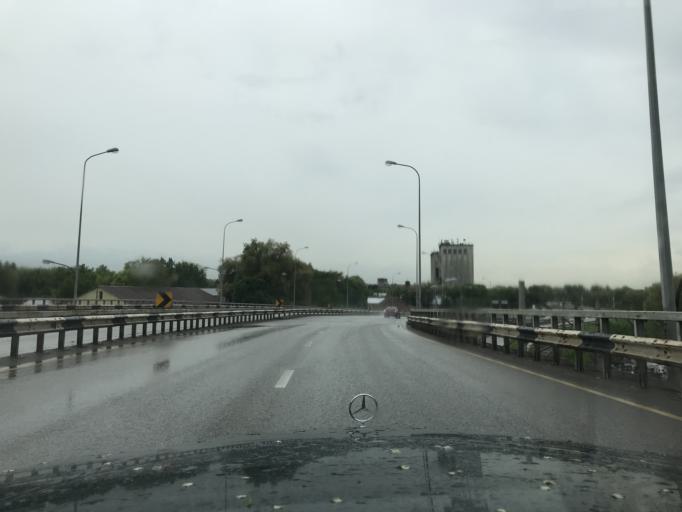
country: KZ
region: Almaty Oblysy
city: Pervomayskiy
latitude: 43.3357
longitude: 76.9632
